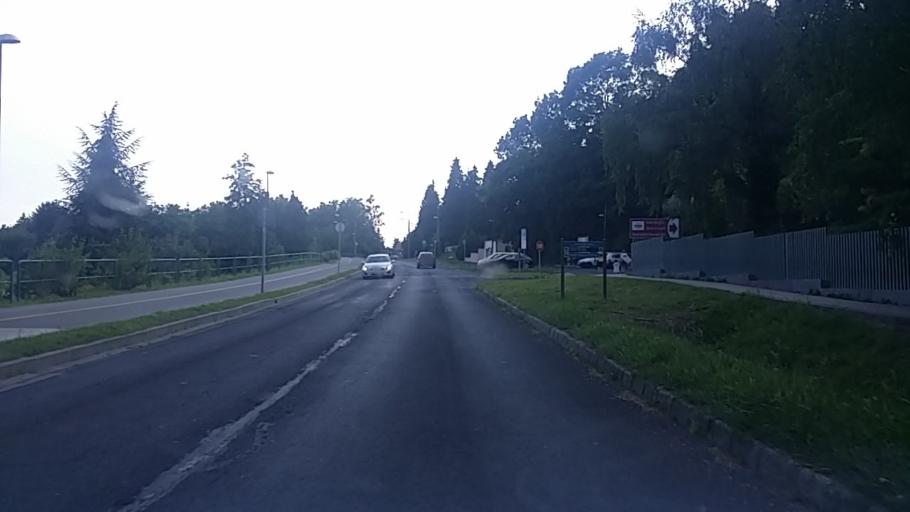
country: HU
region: Zala
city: Heviz
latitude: 46.7838
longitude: 17.1914
